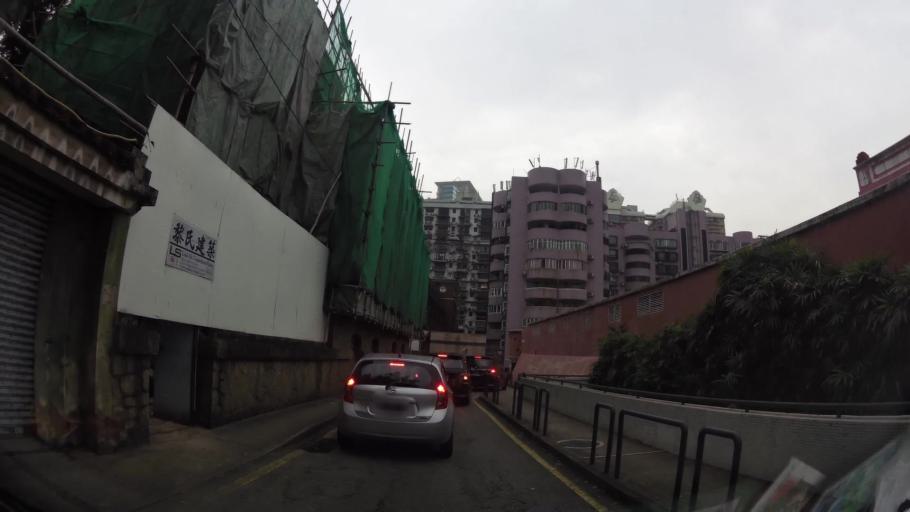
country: MO
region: Macau
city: Macau
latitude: 22.1925
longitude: 113.5454
